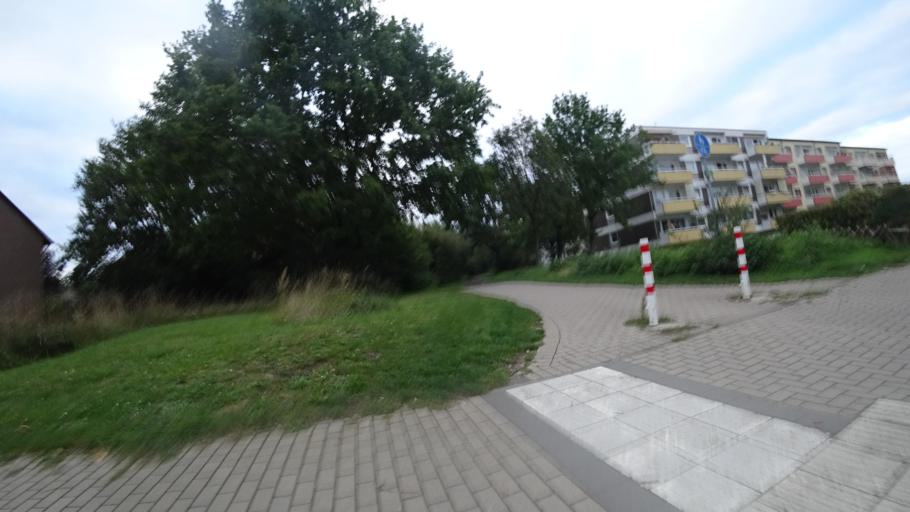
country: DE
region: North Rhine-Westphalia
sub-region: Regierungsbezirk Detmold
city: Bielefeld
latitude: 52.0452
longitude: 8.5523
